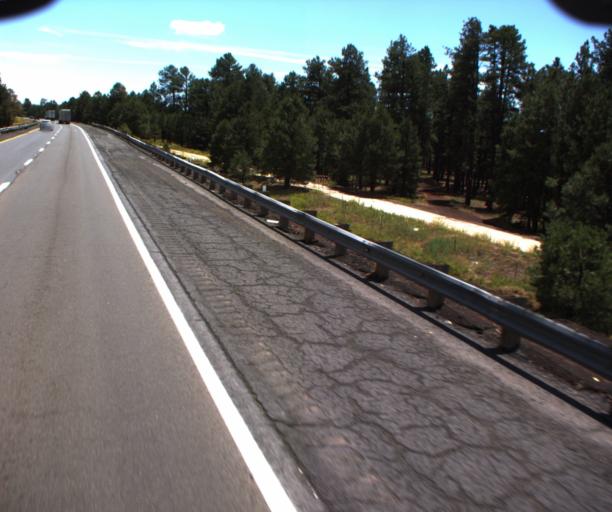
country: US
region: Arizona
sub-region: Coconino County
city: Flagstaff
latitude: 35.2186
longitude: -111.7895
